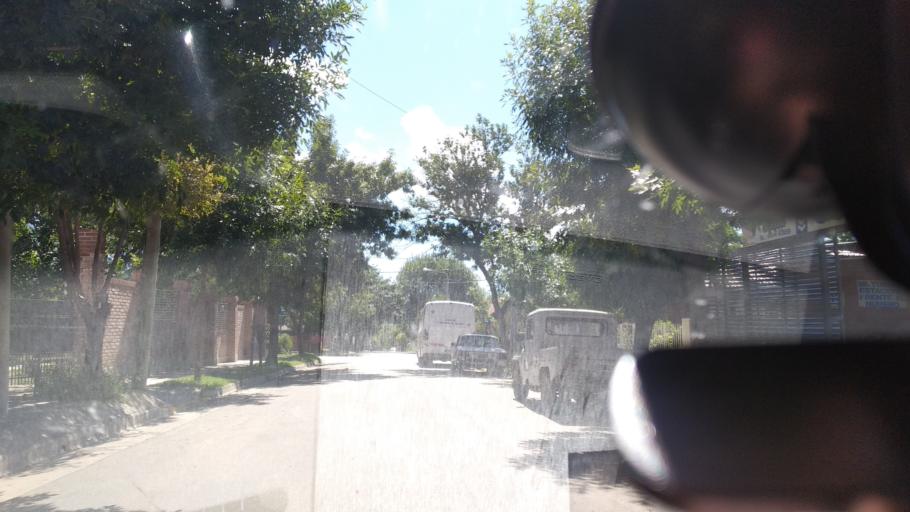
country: AR
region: Cordoba
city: Mina Clavero
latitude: -31.7240
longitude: -65.0076
